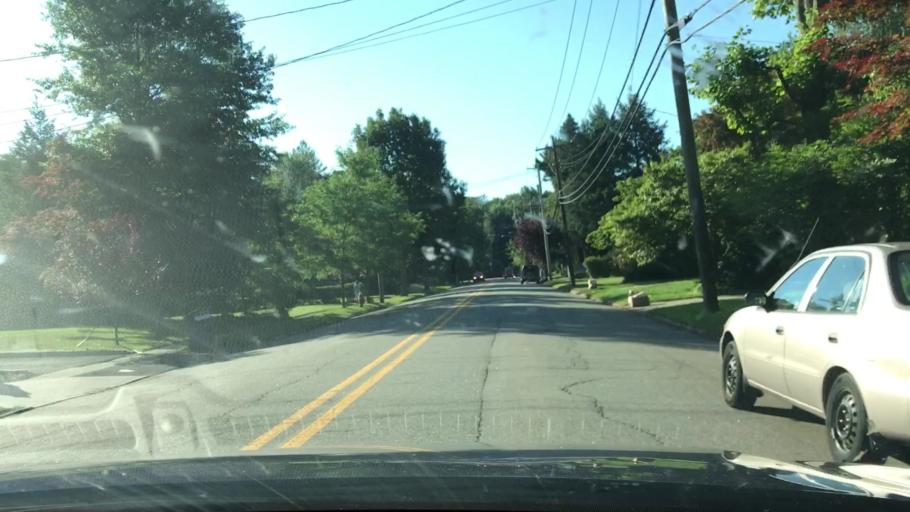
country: US
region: New Jersey
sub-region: Bergen County
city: Cresskill
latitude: 40.9397
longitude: -73.9550
